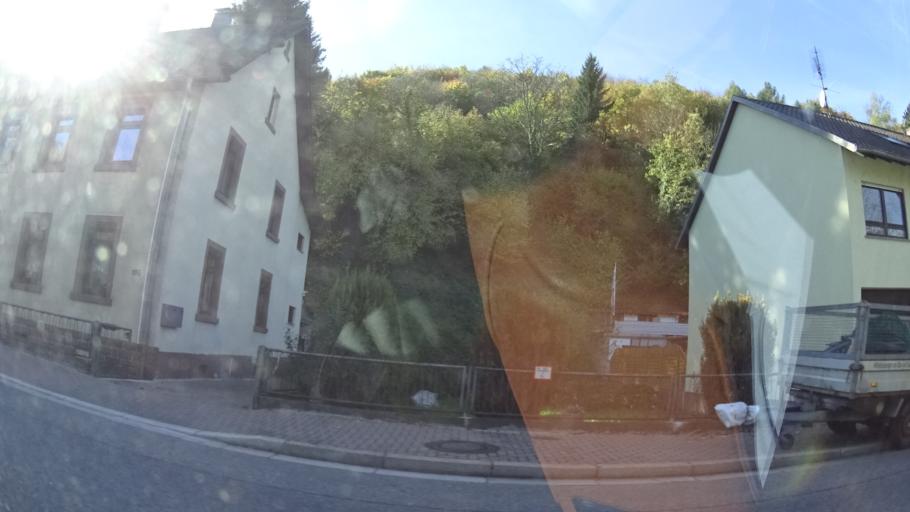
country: DE
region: Baden-Wuerttemberg
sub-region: Karlsruhe Region
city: Joehlingen
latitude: 48.9987
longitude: 8.5316
